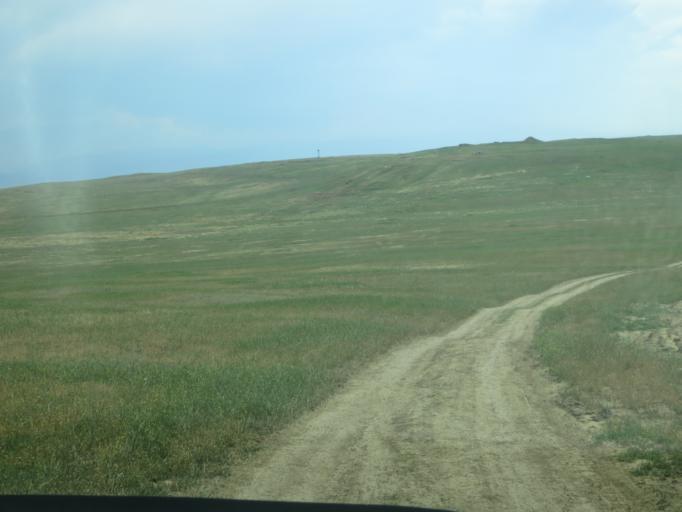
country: AZ
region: Agstafa
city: Saloglu
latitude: 41.4751
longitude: 45.3024
